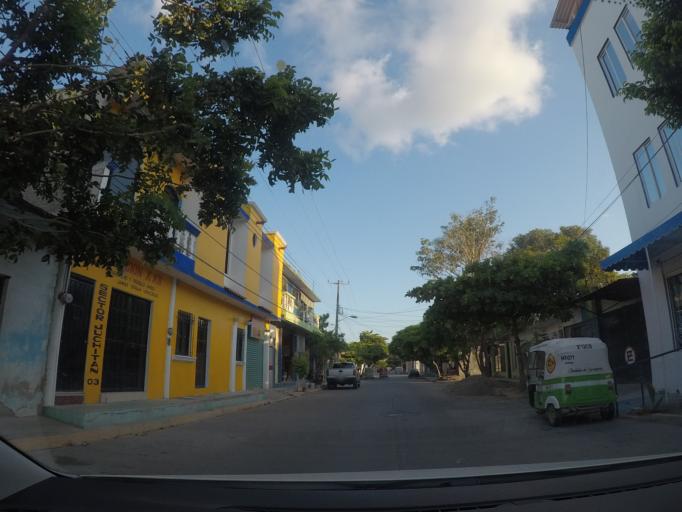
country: MX
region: Oaxaca
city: Juchitan de Zaragoza
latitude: 16.4416
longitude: -95.0207
